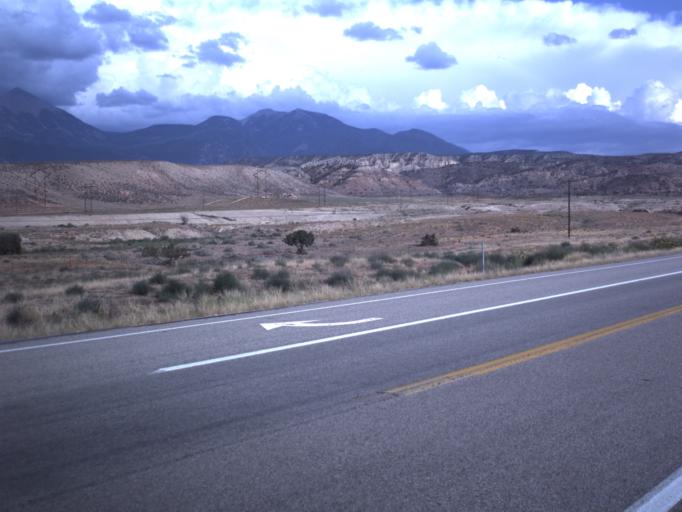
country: US
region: Utah
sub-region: Grand County
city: Moab
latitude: 38.4525
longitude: -109.4391
